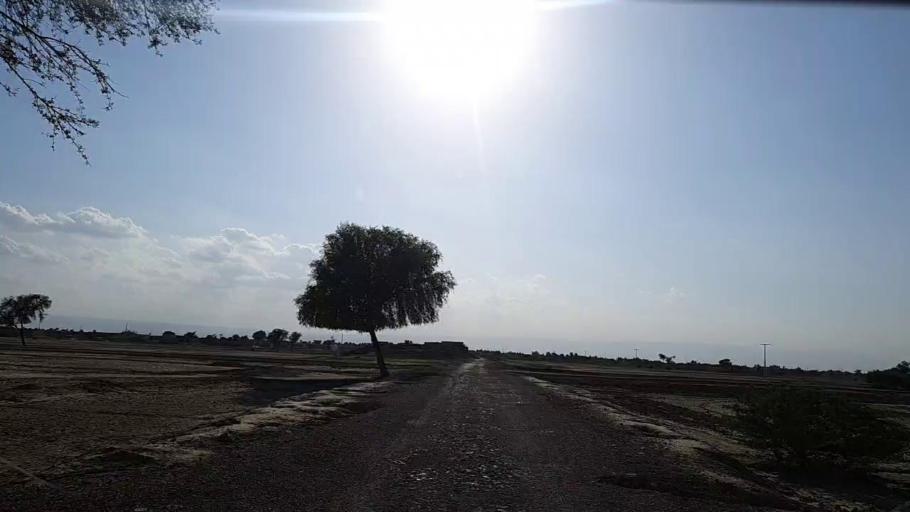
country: PK
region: Sindh
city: Johi
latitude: 26.5846
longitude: 67.5490
